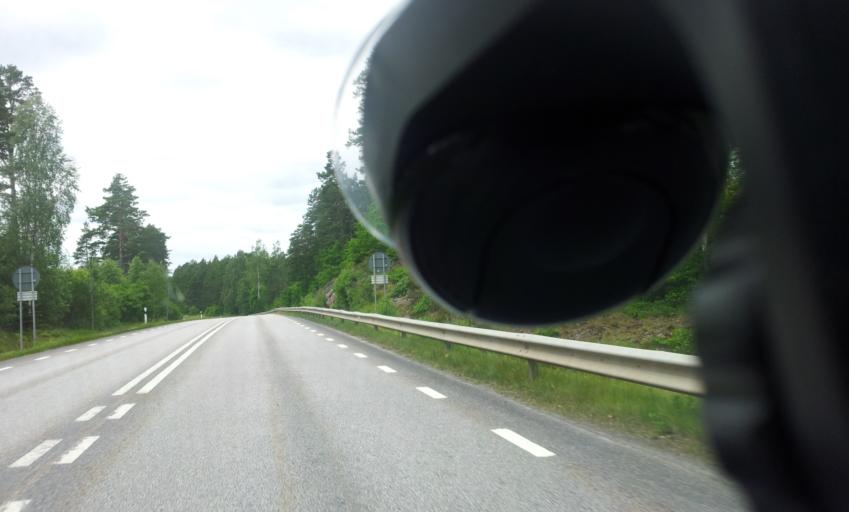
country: SE
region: Kalmar
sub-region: Vasterviks Kommun
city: Vaestervik
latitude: 57.7259
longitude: 16.5116
